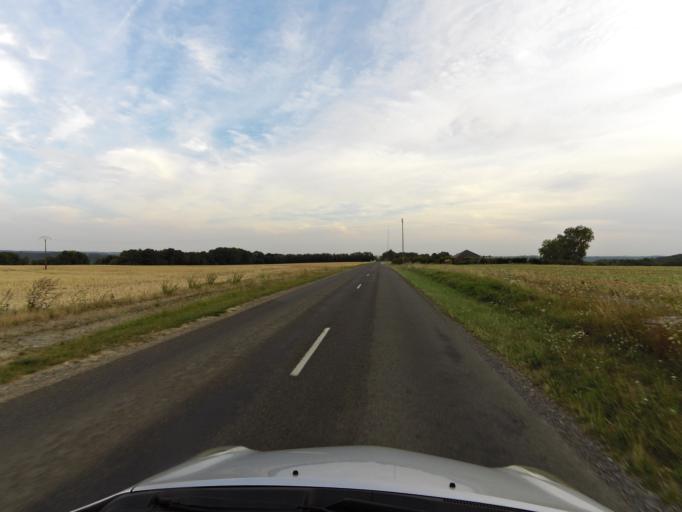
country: FR
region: Picardie
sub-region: Departement de l'Aisne
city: Bruyeres-et-Montberault
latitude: 49.4947
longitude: 3.6698
